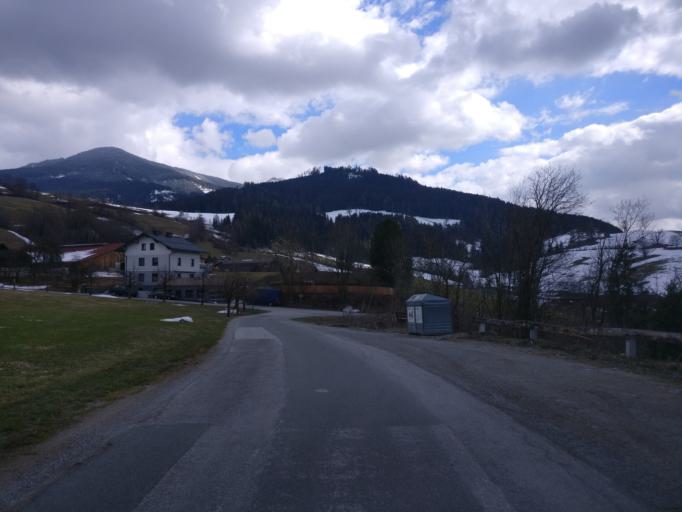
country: AT
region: Salzburg
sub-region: Politischer Bezirk Sankt Johann im Pongau
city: Bischofshofen
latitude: 47.4238
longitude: 13.2344
